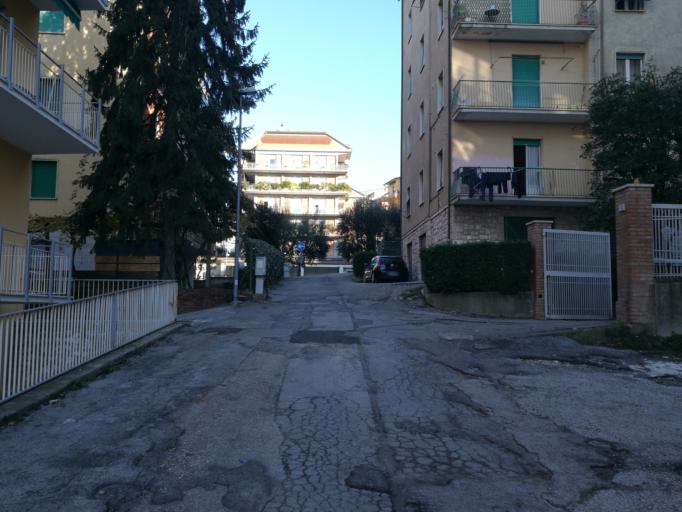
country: IT
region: Umbria
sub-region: Provincia di Perugia
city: Perugia
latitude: 43.0994
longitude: 12.3903
